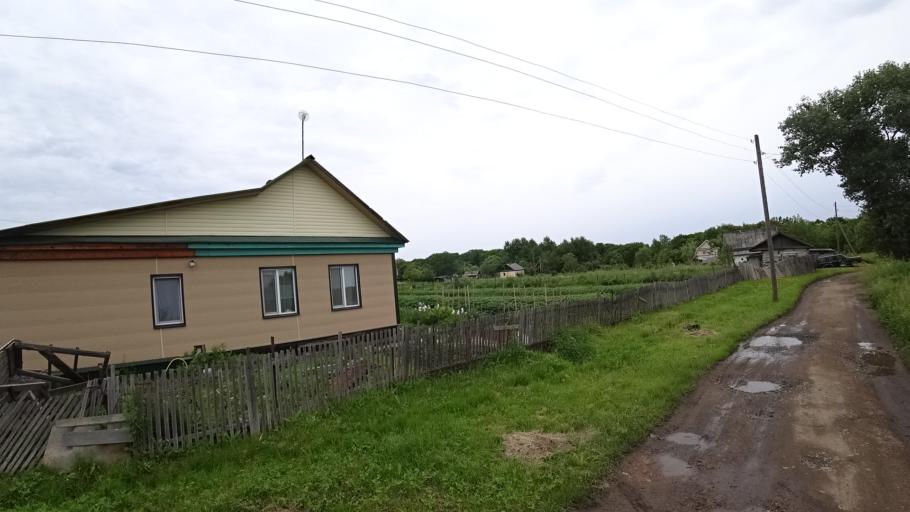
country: RU
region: Primorskiy
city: Novosysoyevka
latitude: 44.2090
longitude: 133.3381
